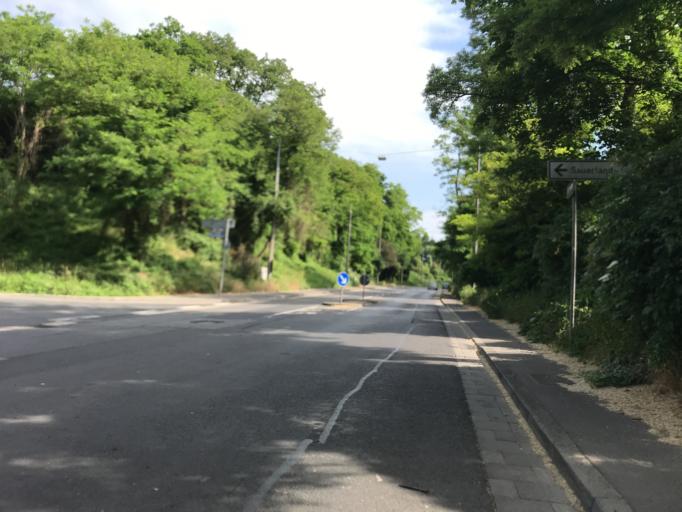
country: DE
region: Hesse
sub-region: Regierungsbezirk Darmstadt
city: Wiesbaden
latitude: 50.0569
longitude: 8.2101
